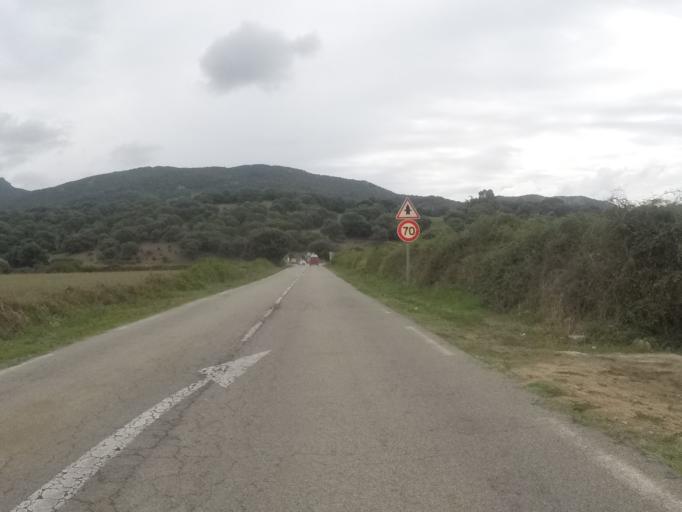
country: FR
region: Corsica
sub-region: Departement de la Corse-du-Sud
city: Propriano
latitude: 41.7223
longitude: 8.8367
